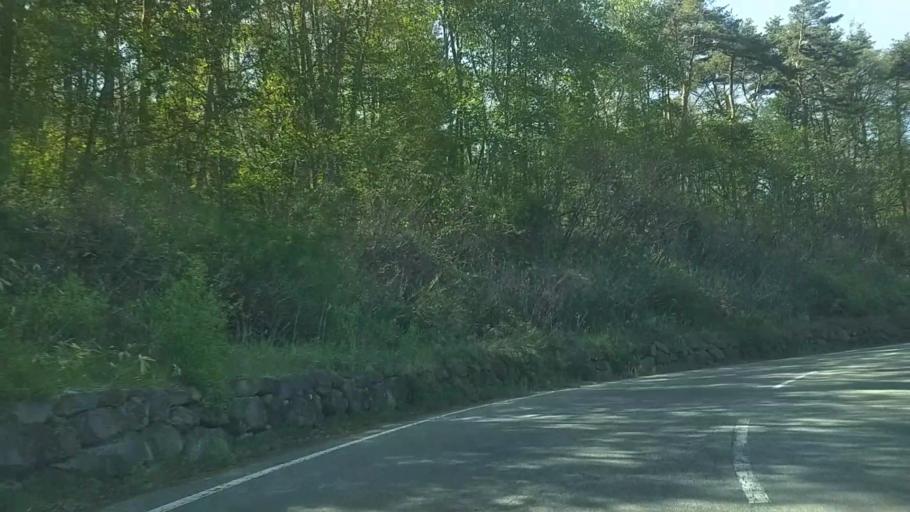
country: JP
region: Yamanashi
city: Nirasaki
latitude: 35.9171
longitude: 138.4323
